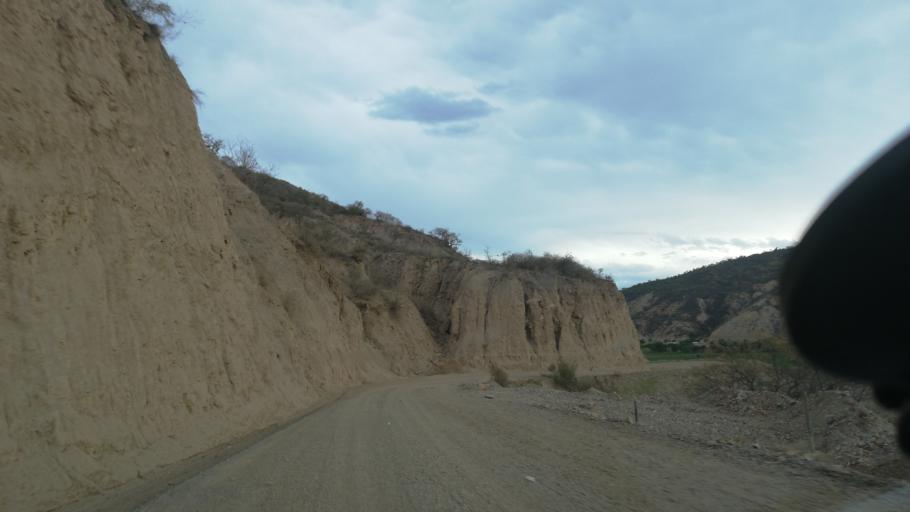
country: BO
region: Cochabamba
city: Sipe Sipe
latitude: -17.5630
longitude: -66.3749
